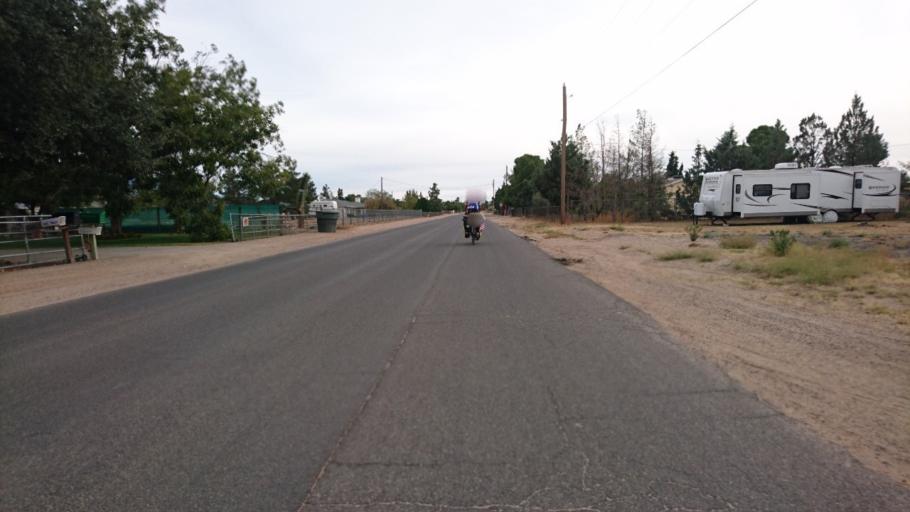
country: US
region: Arizona
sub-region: Mohave County
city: New Kingman-Butler
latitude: 35.2385
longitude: -114.0182
